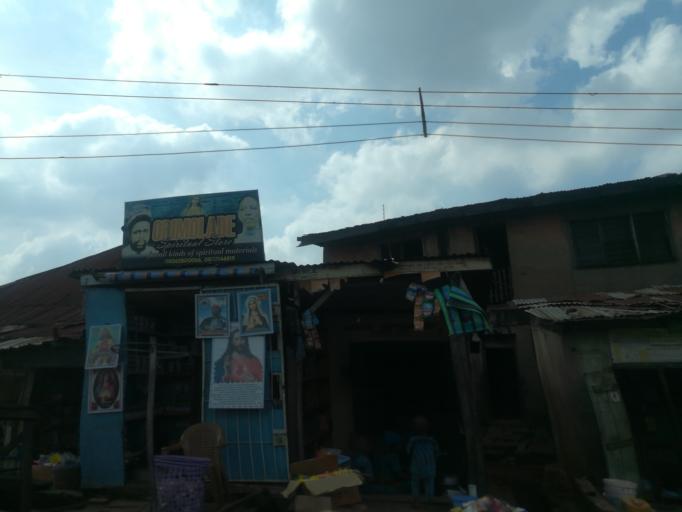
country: NG
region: Oyo
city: Ibadan
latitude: 7.3790
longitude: 3.8968
